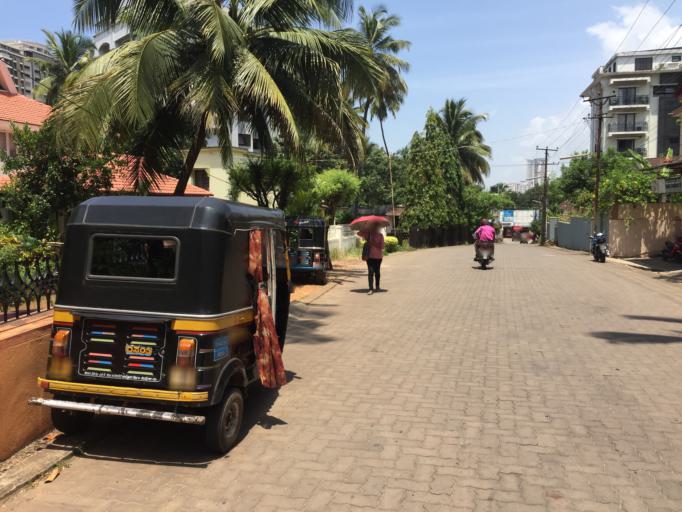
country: IN
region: Karnataka
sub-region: Dakshina Kannada
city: Mangalore
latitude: 12.8774
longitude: 74.8516
